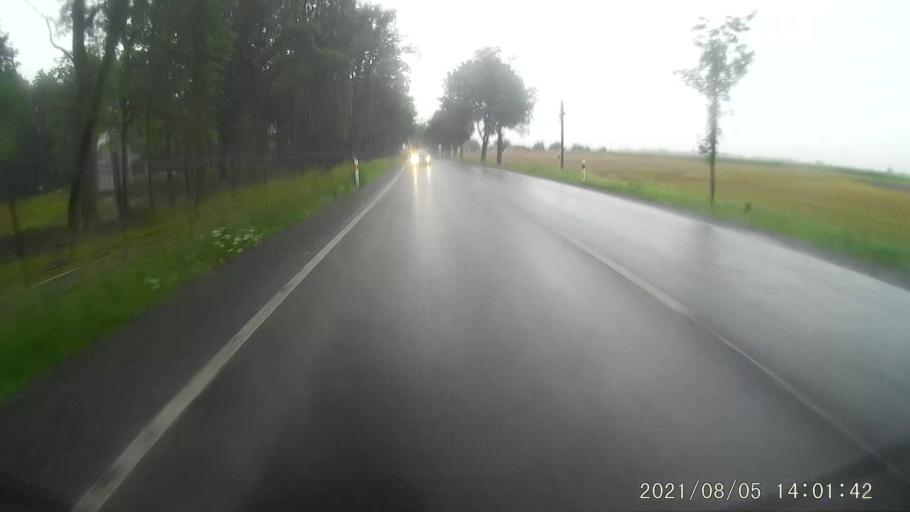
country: PL
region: Opole Voivodeship
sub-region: Powiat krapkowicki
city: Strzeleczki
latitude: 50.4497
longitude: 17.8882
